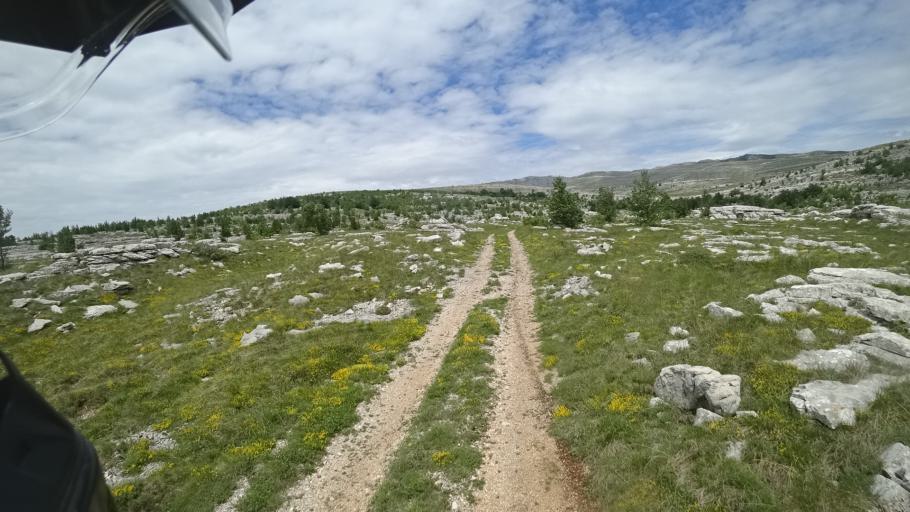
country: HR
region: Splitsko-Dalmatinska
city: Hrvace
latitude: 43.8913
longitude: 16.5849
